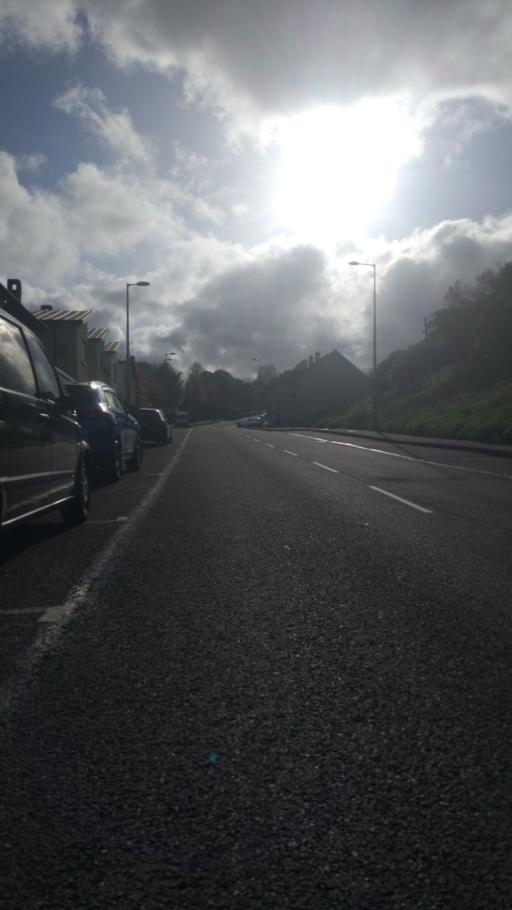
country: IE
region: Munster
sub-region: County Cork
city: Cork
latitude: 51.9066
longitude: -8.4823
